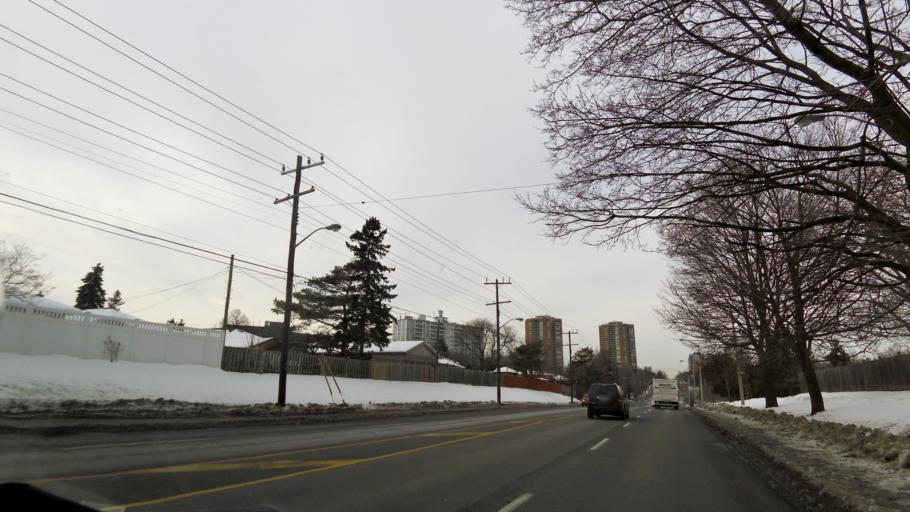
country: CA
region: Ontario
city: Etobicoke
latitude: 43.6931
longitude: -79.5448
